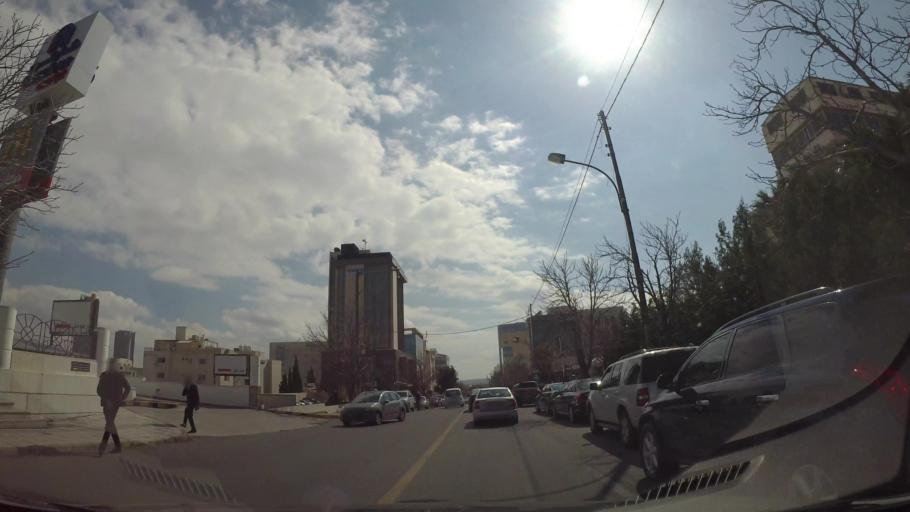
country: JO
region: Amman
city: Amman
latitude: 31.9708
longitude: 35.8965
